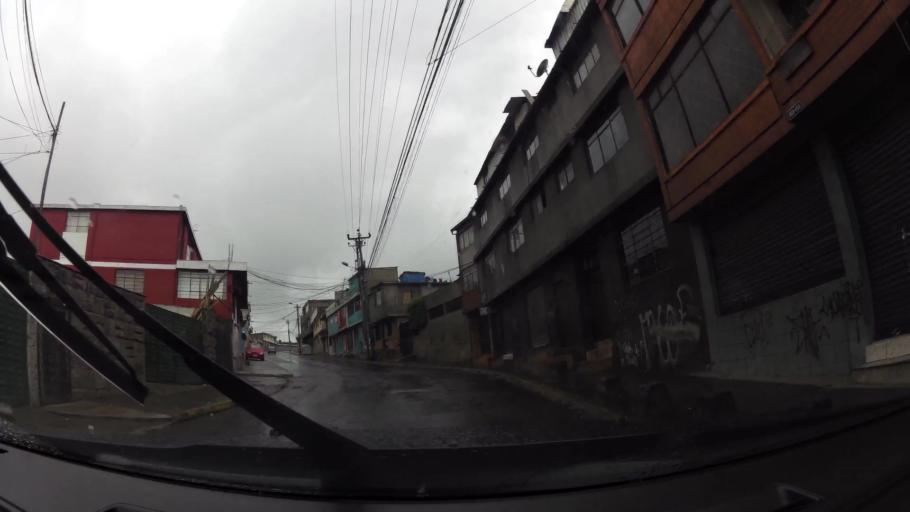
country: EC
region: Pichincha
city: Quito
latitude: -0.1077
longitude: -78.4970
